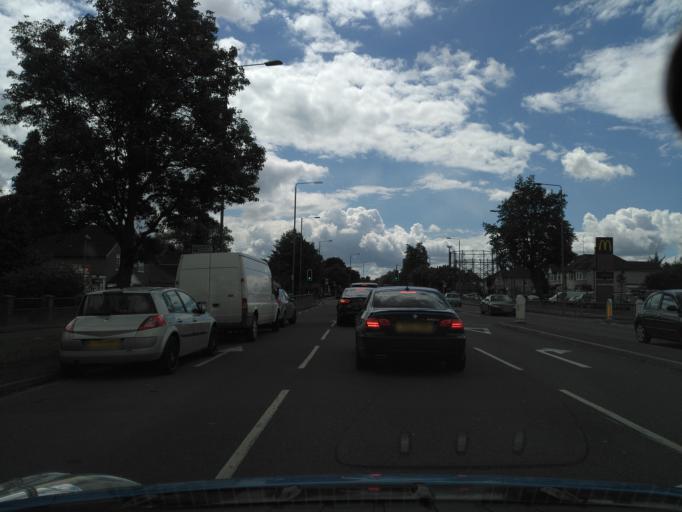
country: GB
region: England
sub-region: Greater London
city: Sidcup
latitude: 51.4028
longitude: 0.1132
